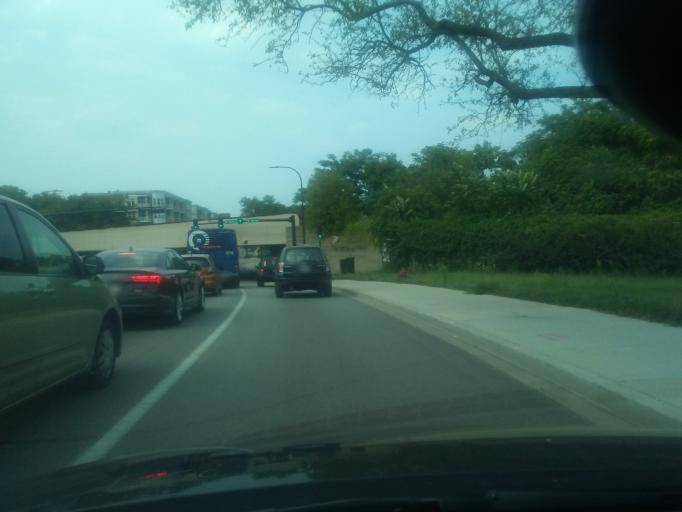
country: US
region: Illinois
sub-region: Cook County
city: Evanston
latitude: 42.0509
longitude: -87.6880
